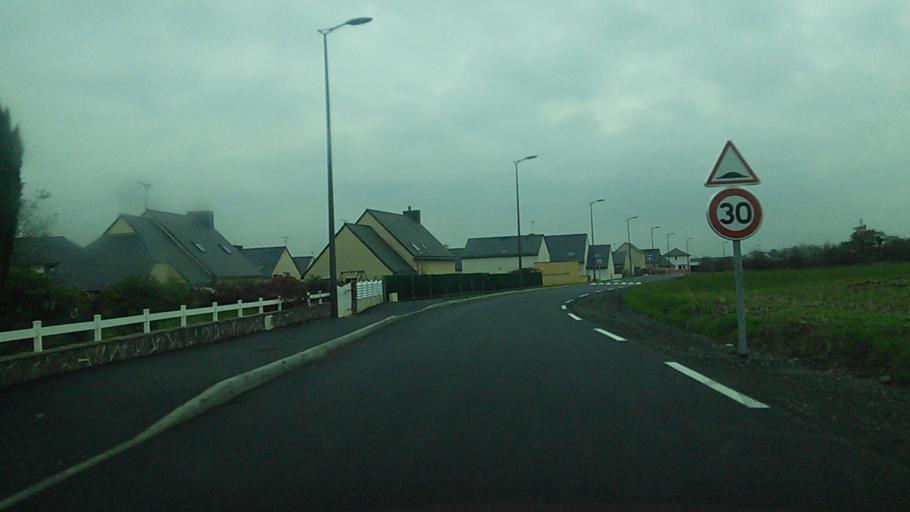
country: FR
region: Brittany
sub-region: Departement des Cotes-d'Armor
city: Yffiniac
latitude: 48.4818
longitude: -2.6583
